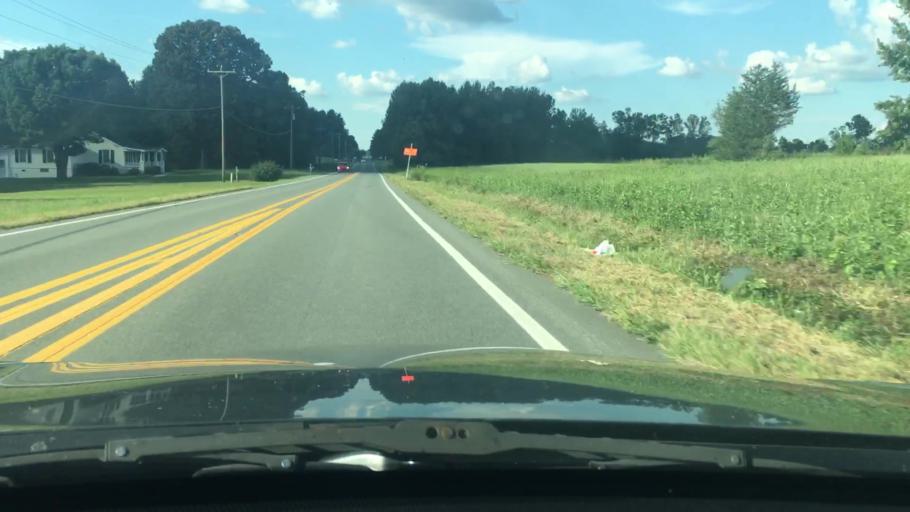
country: US
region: North Carolina
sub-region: Alamance County
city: Green Level
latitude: 36.2016
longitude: -79.3225
